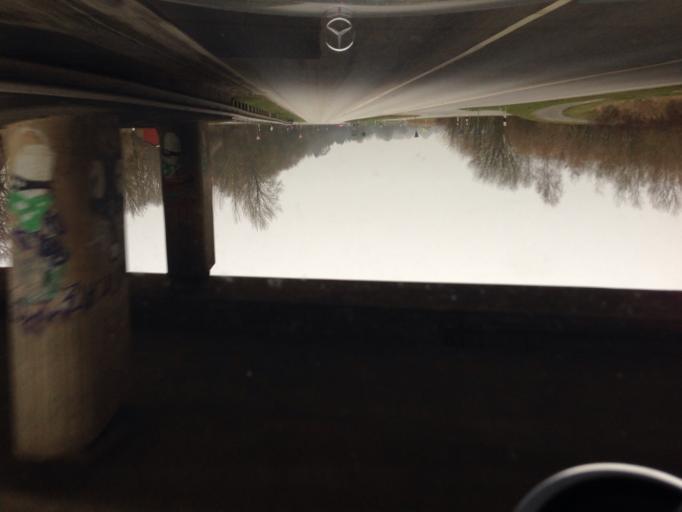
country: DE
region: Schleswig-Holstein
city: Kirchbarkau
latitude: 54.2239
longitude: 10.1462
